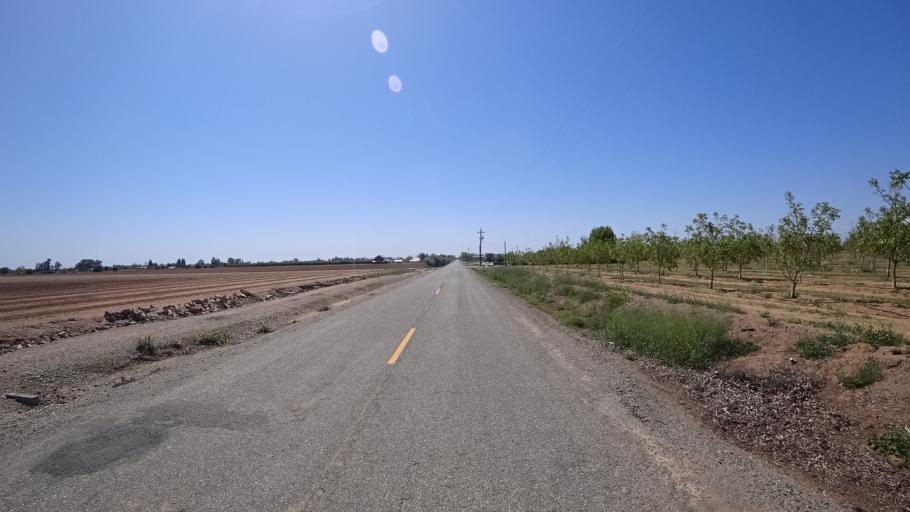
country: US
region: California
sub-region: Glenn County
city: Orland
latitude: 39.7809
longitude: -122.1690
